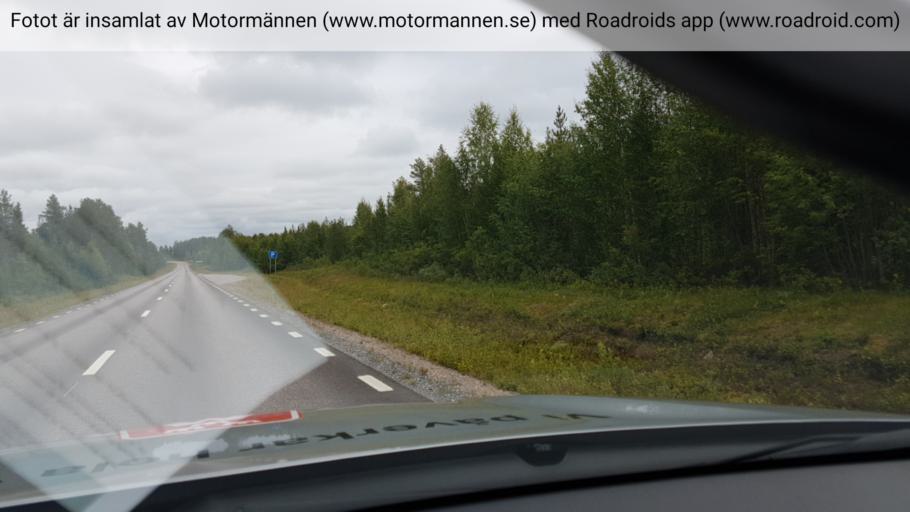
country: SE
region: Norrbotten
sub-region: Gallivare Kommun
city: Gaellivare
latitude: 67.0678
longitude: 21.3068
